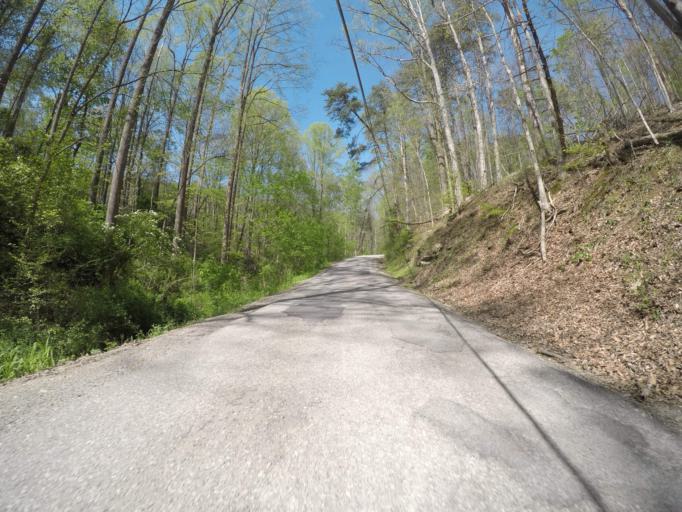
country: US
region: West Virginia
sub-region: Kanawha County
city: Charleston
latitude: 38.4150
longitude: -81.5958
